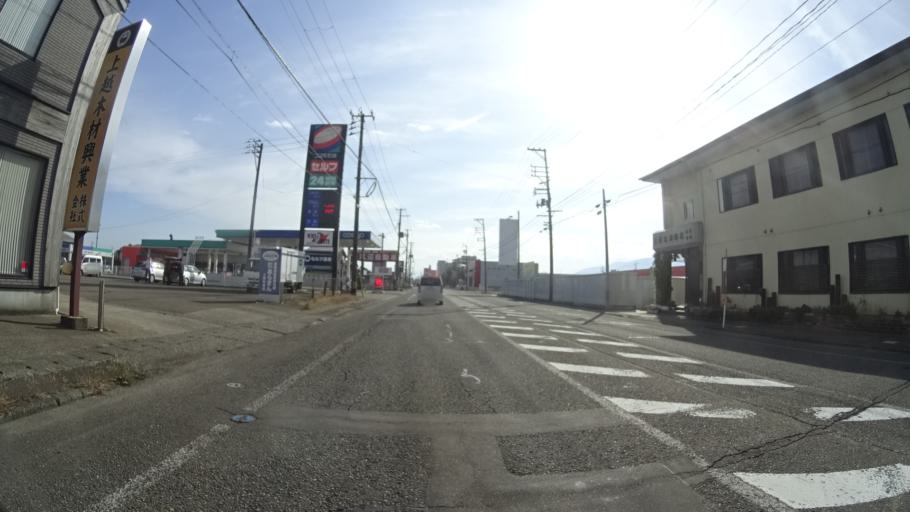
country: JP
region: Niigata
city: Joetsu
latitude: 37.1559
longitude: 138.2381
